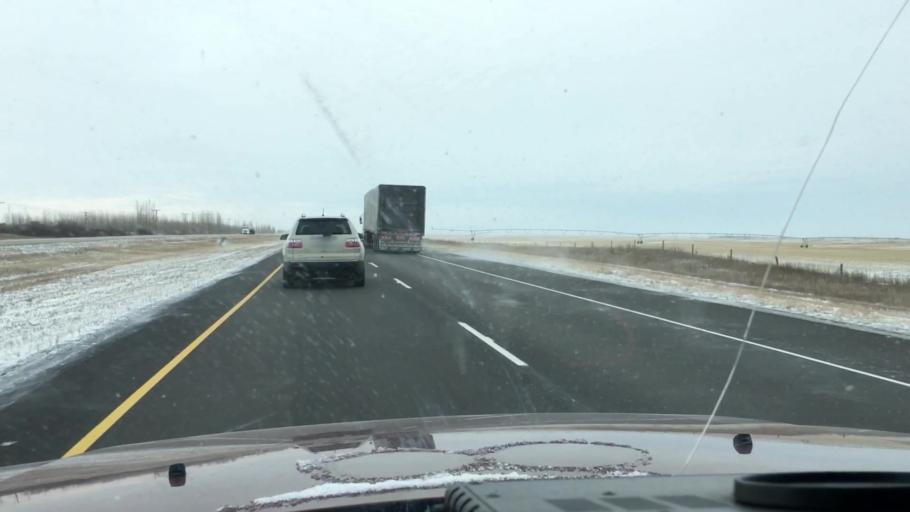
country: CA
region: Saskatchewan
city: Saskatoon
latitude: 51.7753
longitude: -106.4764
